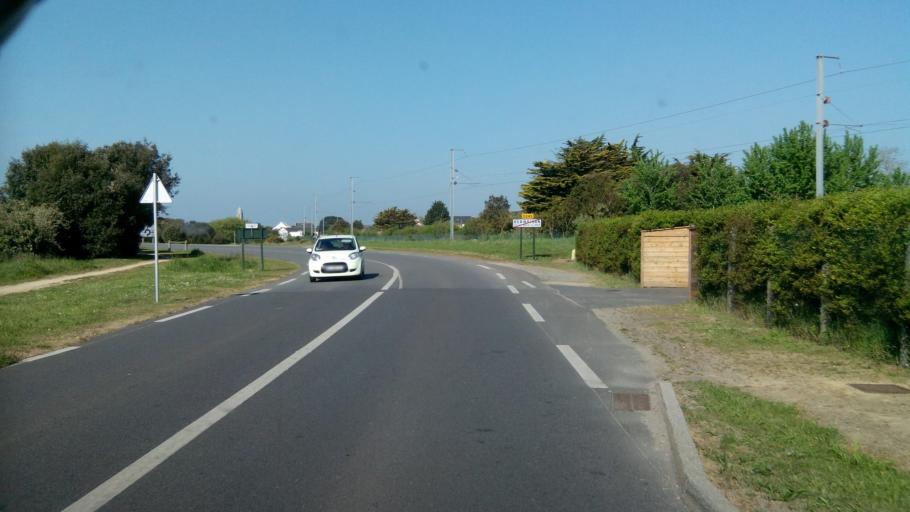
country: FR
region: Pays de la Loire
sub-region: Departement de la Loire-Atlantique
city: Batz-sur-Mer
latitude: 47.2786
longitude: -2.4560
